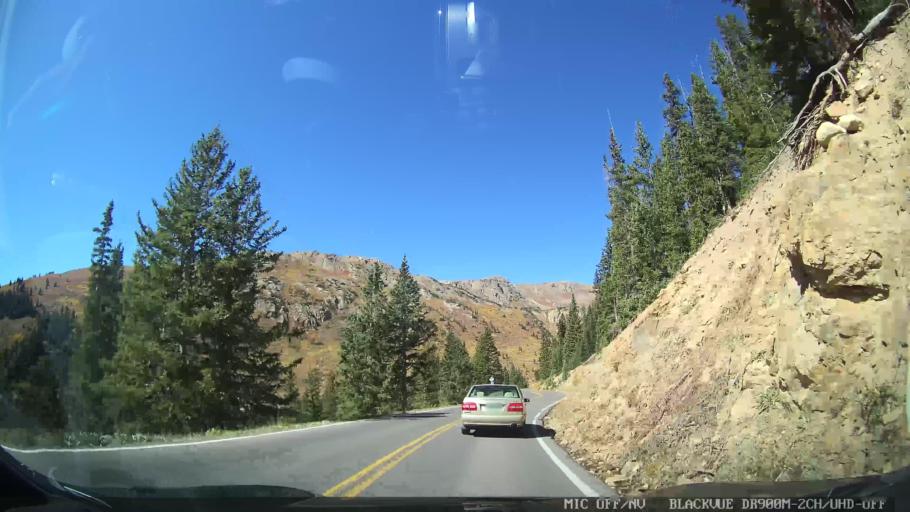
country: US
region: Colorado
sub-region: Pitkin County
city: Aspen
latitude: 39.1201
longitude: -106.5748
